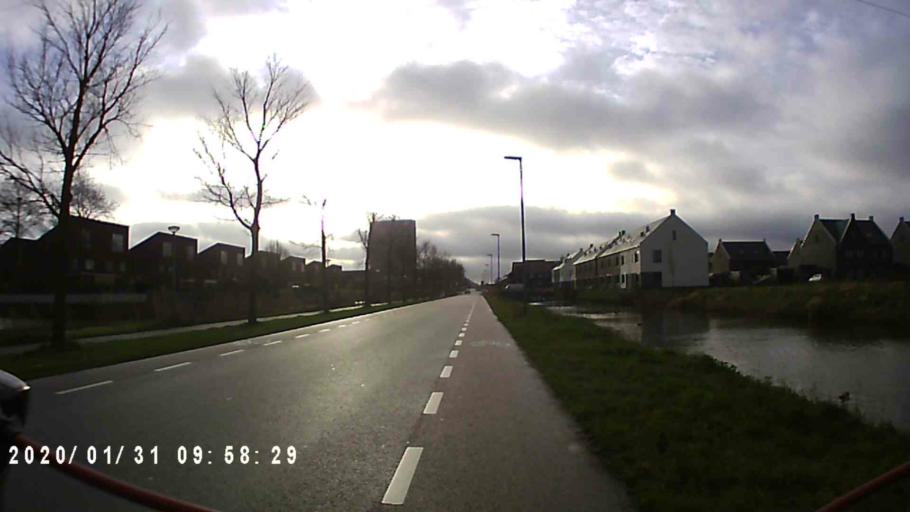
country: NL
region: Groningen
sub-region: Gemeente Groningen
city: Korrewegwijk
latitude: 53.2395
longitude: 6.5234
